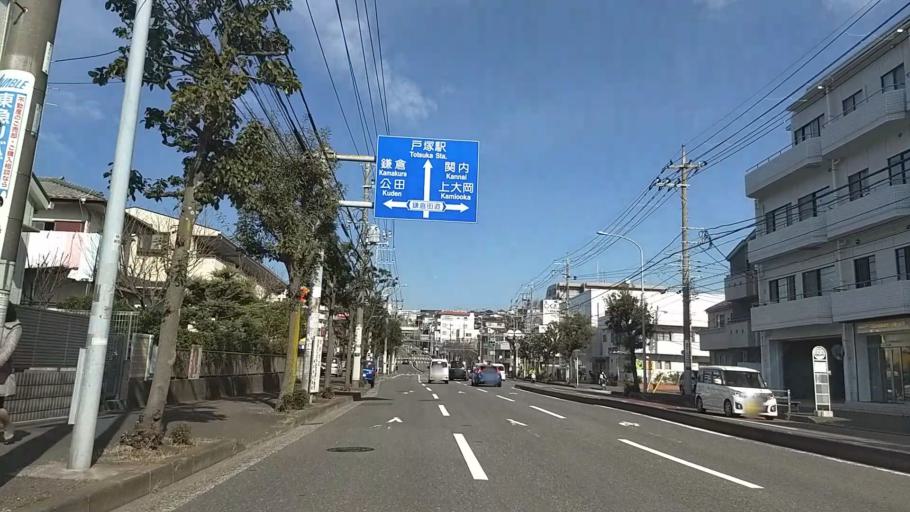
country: JP
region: Kanagawa
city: Kamakura
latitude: 35.3817
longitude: 139.5780
